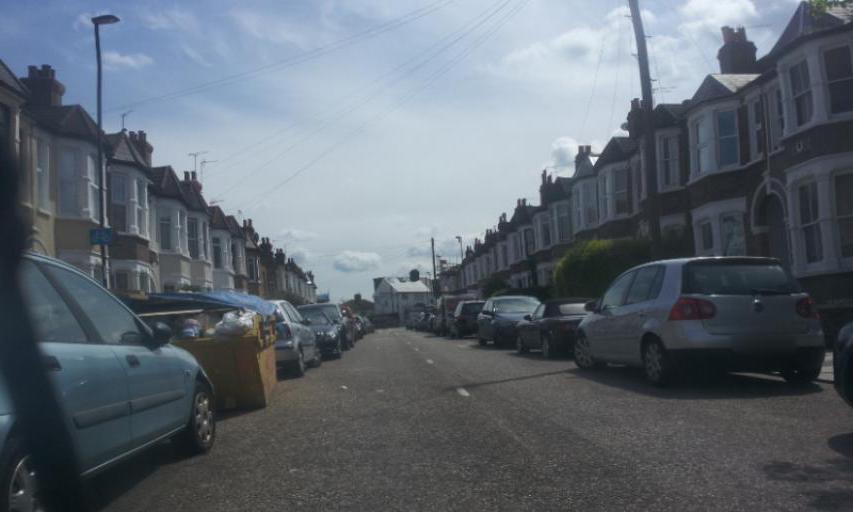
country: GB
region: England
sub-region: Greater London
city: Catford
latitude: 51.4512
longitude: -0.0314
